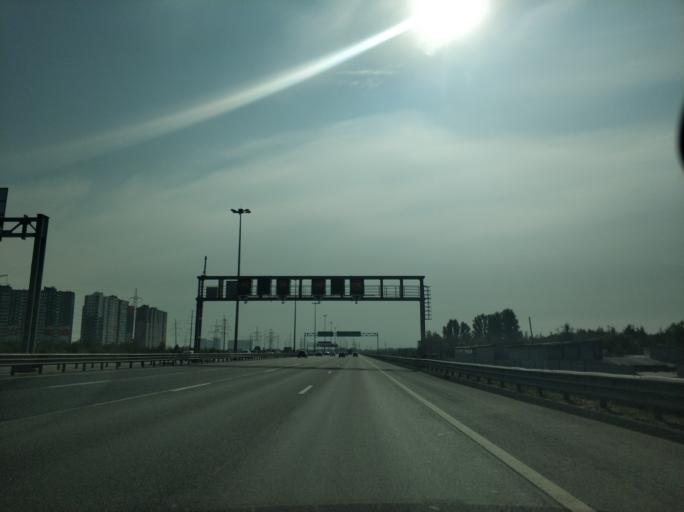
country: RU
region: Leningrad
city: Murino
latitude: 60.0301
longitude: 30.4451
